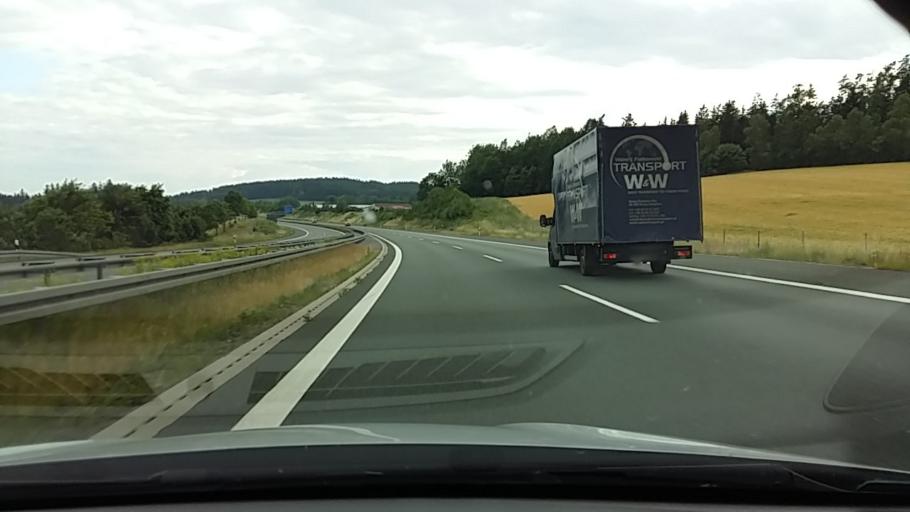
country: DE
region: Bavaria
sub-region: Upper Palatinate
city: Leuchtenberg
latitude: 49.5855
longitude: 12.2802
